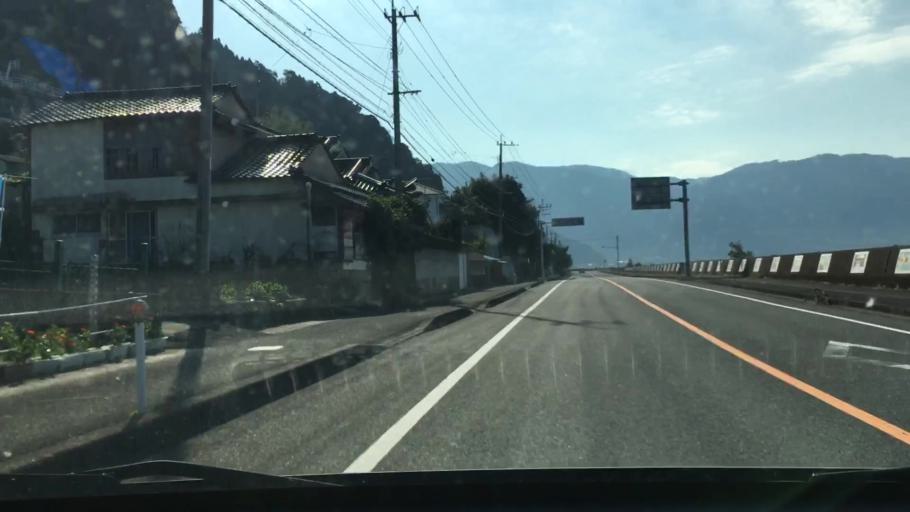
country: JP
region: Kagoshima
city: Kokubu-matsuki
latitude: 31.6683
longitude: 130.8194
